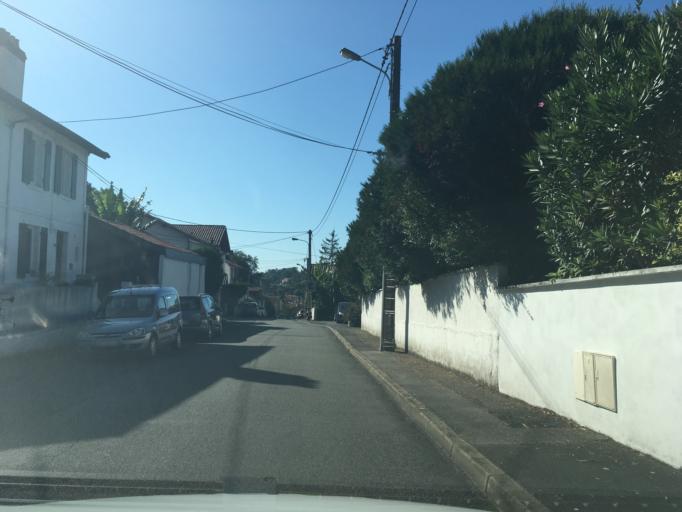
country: FR
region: Aquitaine
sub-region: Departement des Pyrenees-Atlantiques
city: Biarritz
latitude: 43.4581
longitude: -1.5416
